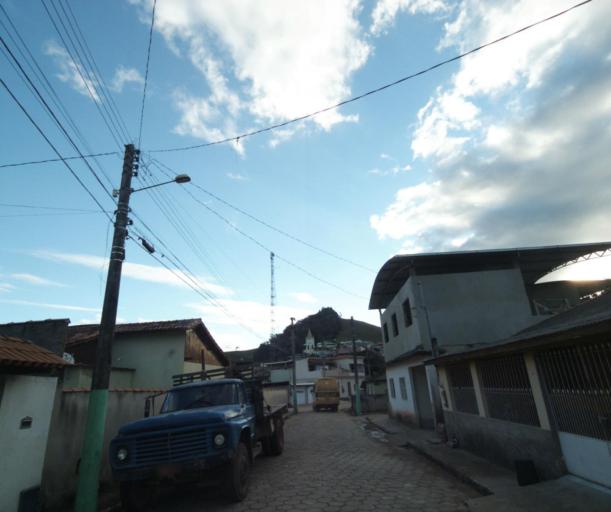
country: BR
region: Espirito Santo
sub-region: Guacui
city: Guacui
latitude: -20.6186
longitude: -41.6828
